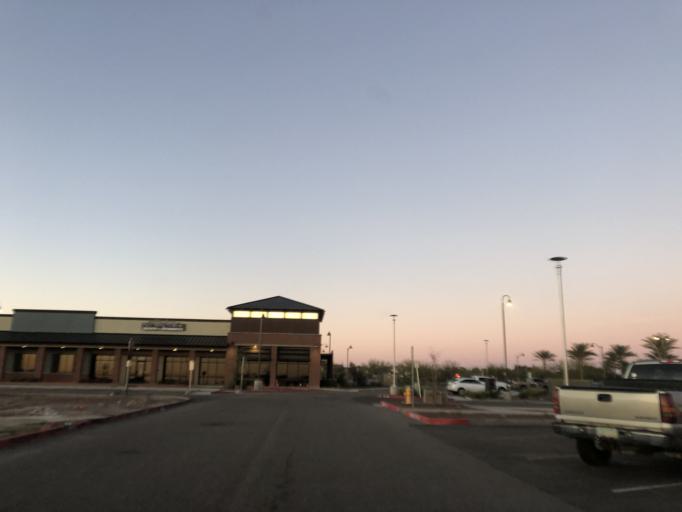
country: US
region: Arizona
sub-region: Maricopa County
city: Citrus Park
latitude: 33.4658
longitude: -112.5057
